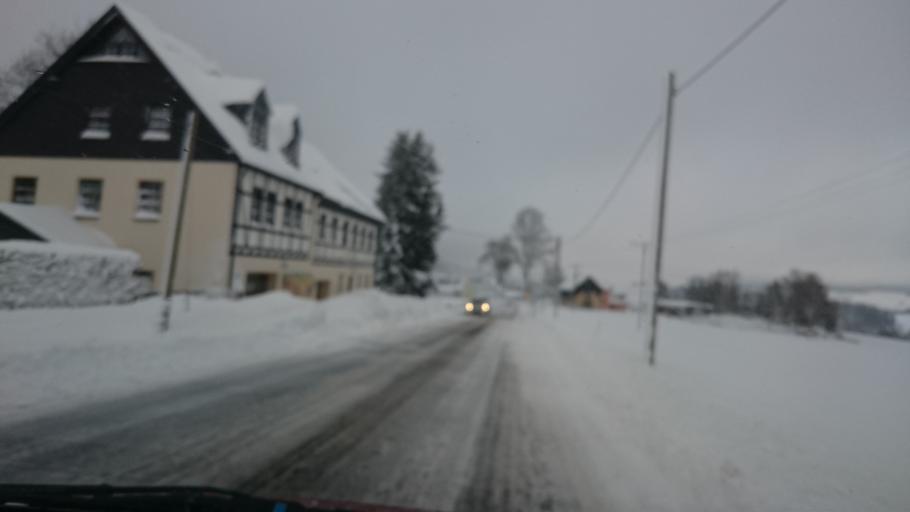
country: DE
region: Saxony
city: Geyer
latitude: 50.6163
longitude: 12.9161
